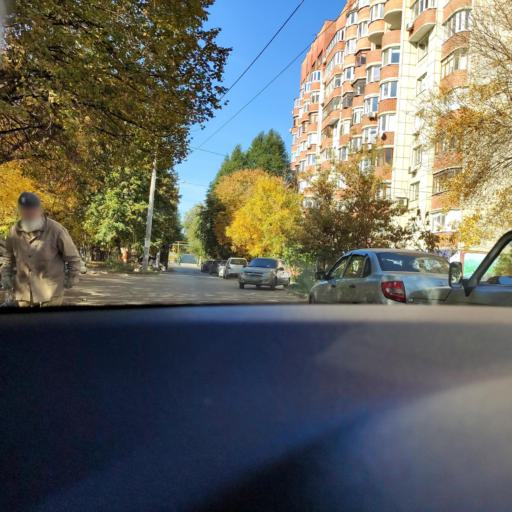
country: RU
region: Samara
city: Petra-Dubrava
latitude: 53.2383
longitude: 50.2766
